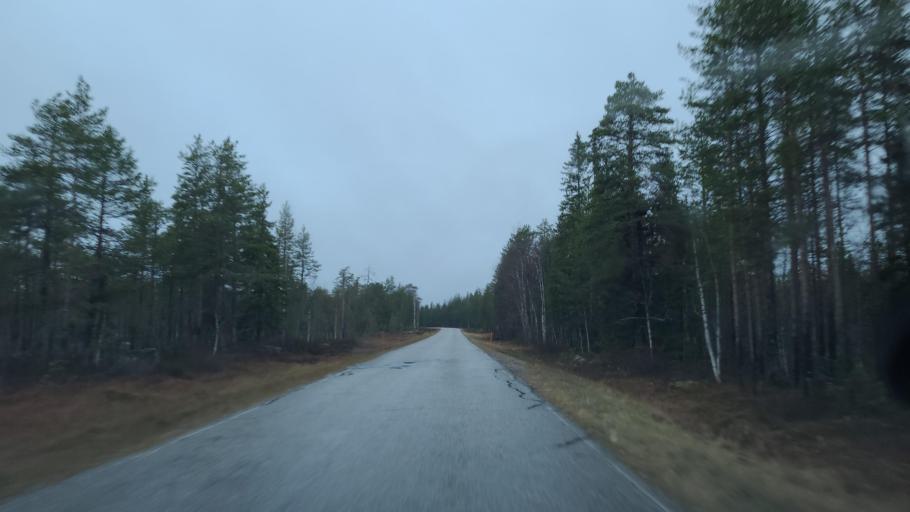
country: FI
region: Lapland
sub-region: Kemi-Tornio
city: Simo
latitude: 65.8829
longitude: 25.2213
